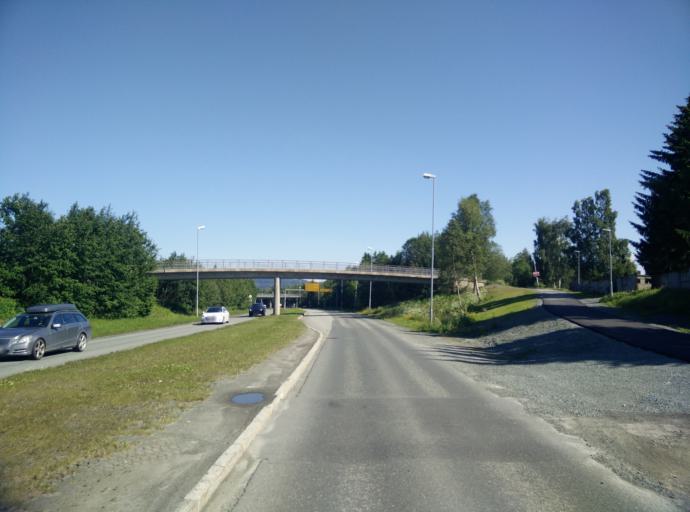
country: NO
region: Sor-Trondelag
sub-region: Trondheim
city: Trondheim
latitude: 63.3710
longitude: 10.3397
